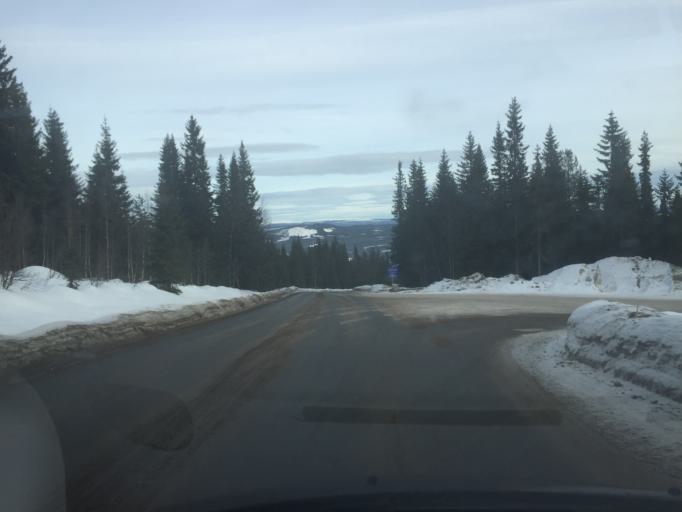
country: NO
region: Hedmark
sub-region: Trysil
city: Innbygda
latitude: 61.3383
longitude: 12.1876
